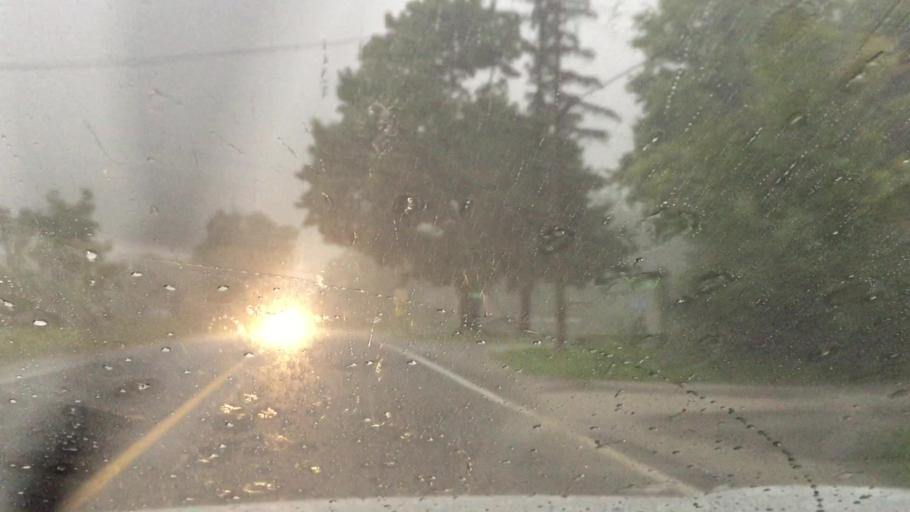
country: CA
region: Ontario
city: Markham
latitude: 43.8566
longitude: -79.2037
